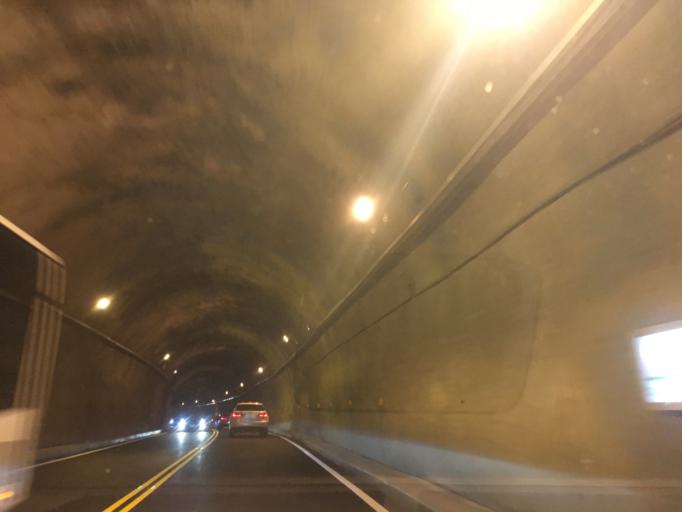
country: TW
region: Taiwan
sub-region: Hualien
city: Hualian
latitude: 24.1723
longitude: 121.5733
